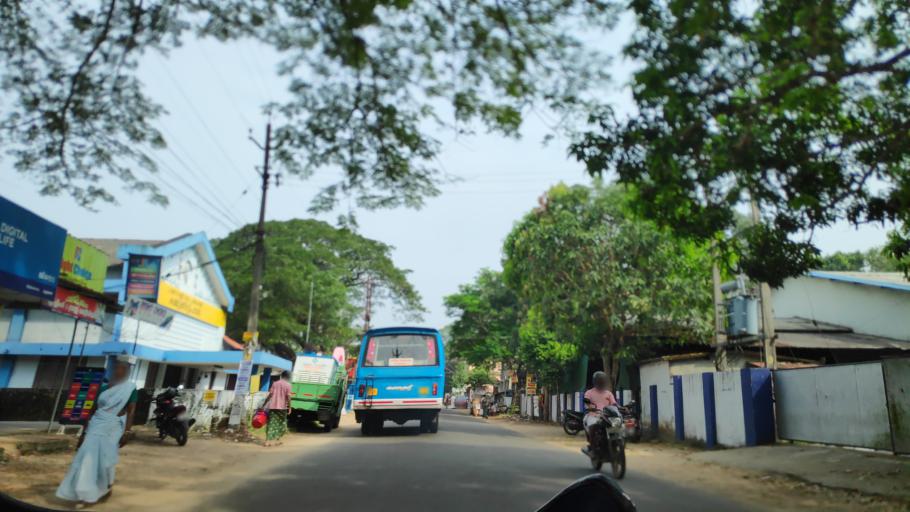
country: IN
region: Kerala
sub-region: Alappuzha
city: Kutiatodu
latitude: 9.8006
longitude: 76.3537
